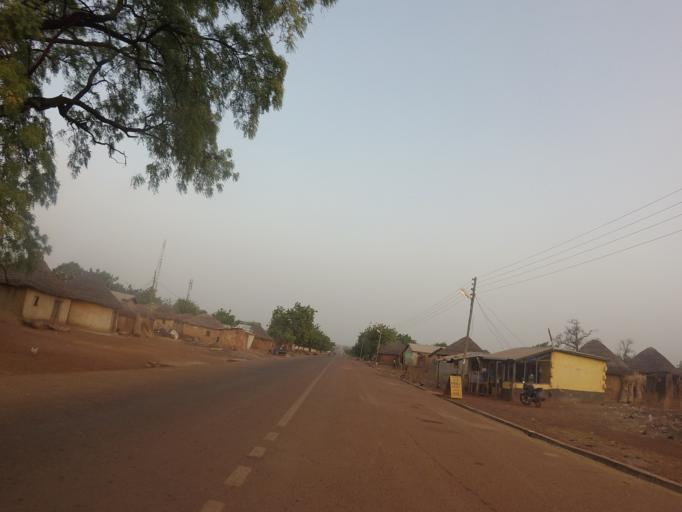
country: GH
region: Northern
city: Tamale
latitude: 9.4449
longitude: -1.1155
